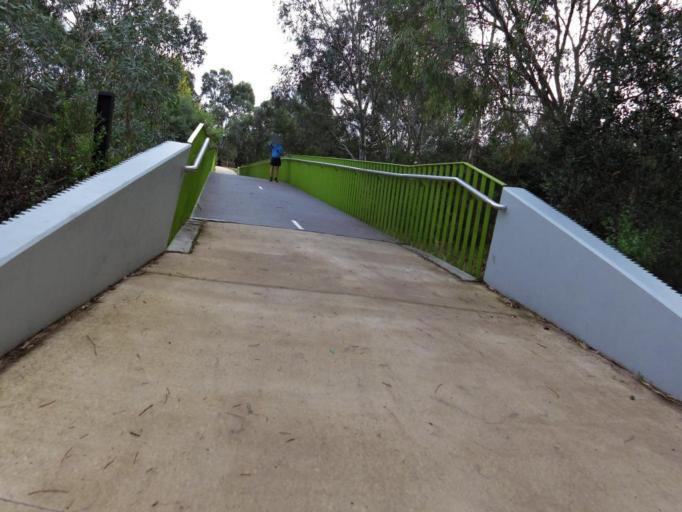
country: AU
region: Victoria
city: Alphington
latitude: -37.7795
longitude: 145.0384
